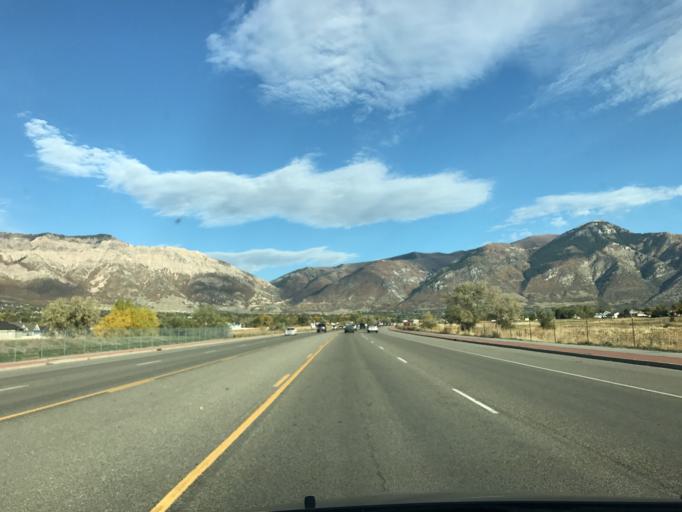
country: US
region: Utah
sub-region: Weber County
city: Pleasant View
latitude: 41.3068
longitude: -111.9995
